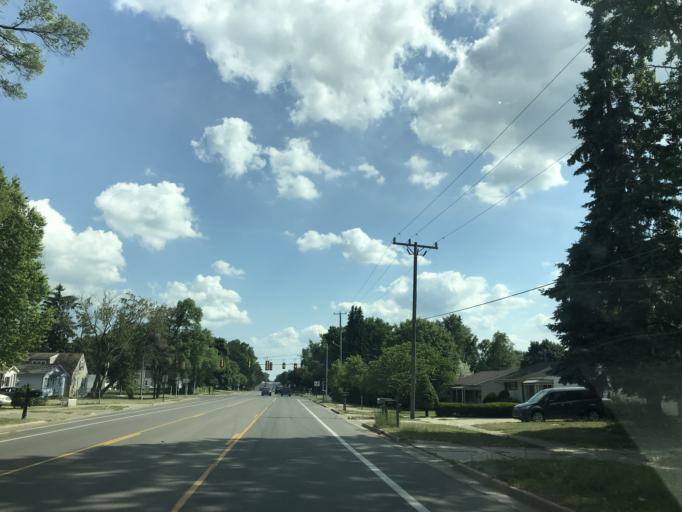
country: US
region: Michigan
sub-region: Washtenaw County
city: Ypsilanti
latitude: 42.2511
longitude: -83.5806
